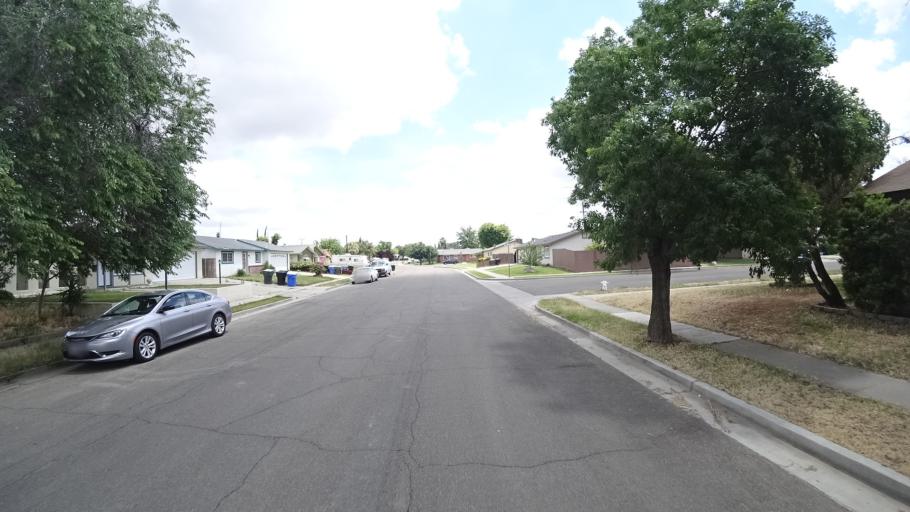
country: US
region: California
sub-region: Kings County
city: Hanford
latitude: 36.3114
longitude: -119.6724
